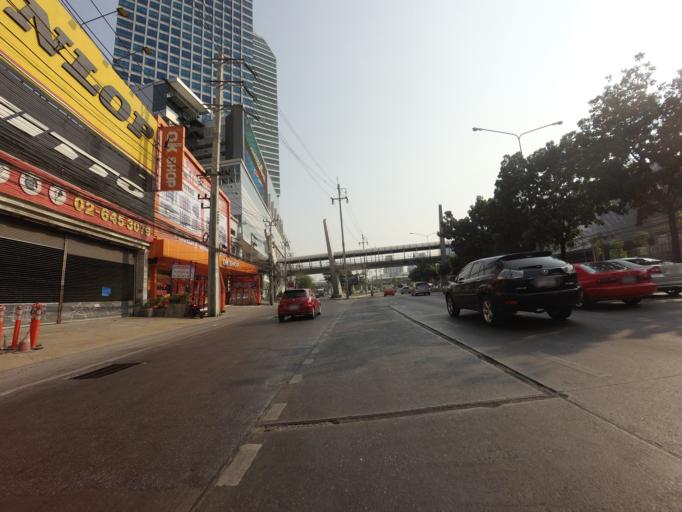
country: TH
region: Bangkok
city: Huai Khwang
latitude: 13.7709
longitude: 100.5734
